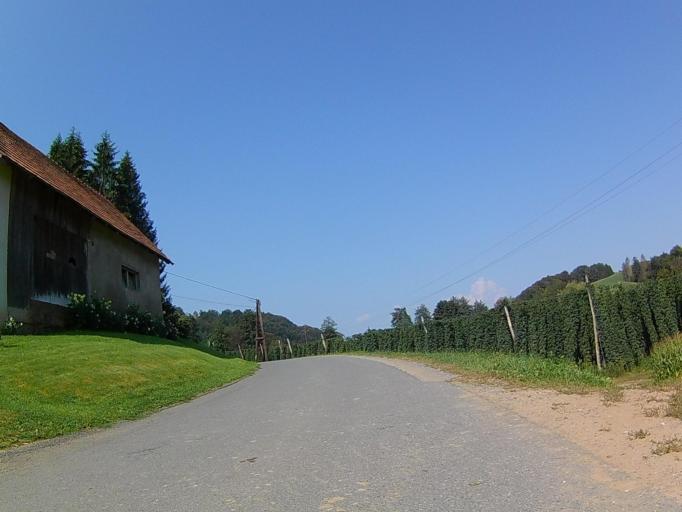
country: AT
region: Styria
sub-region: Politischer Bezirk Leibnitz
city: Leutschach
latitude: 46.6664
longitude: 15.4508
